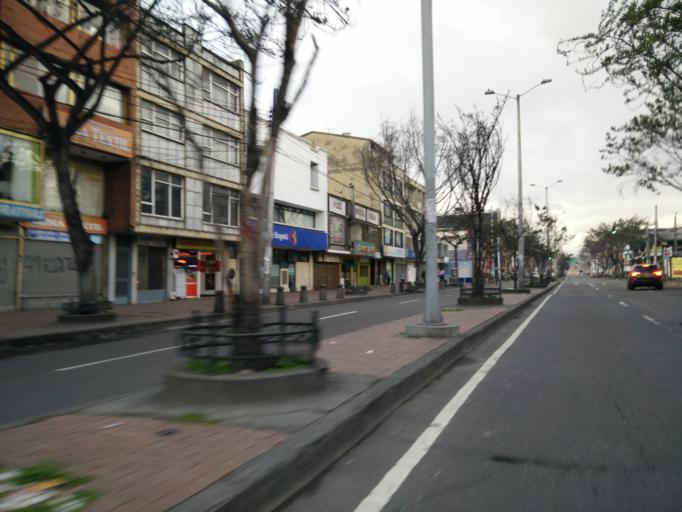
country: CO
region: Bogota D.C.
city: Bogota
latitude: 4.6566
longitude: -74.0712
